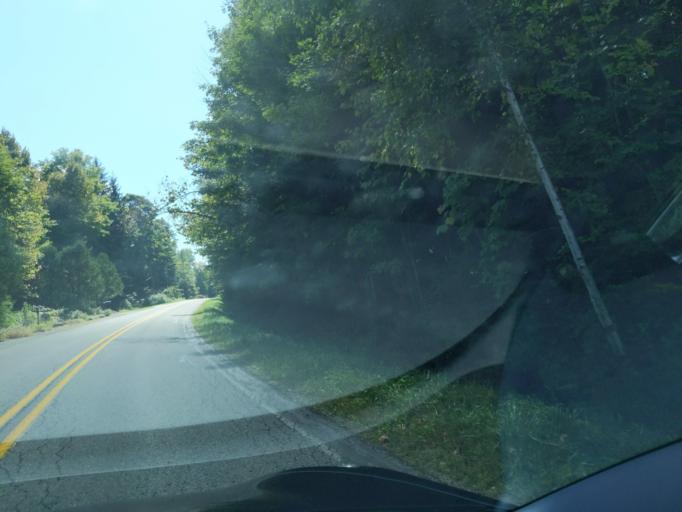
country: US
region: Michigan
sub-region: Antrim County
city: Elk Rapids
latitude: 44.9576
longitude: -85.3236
